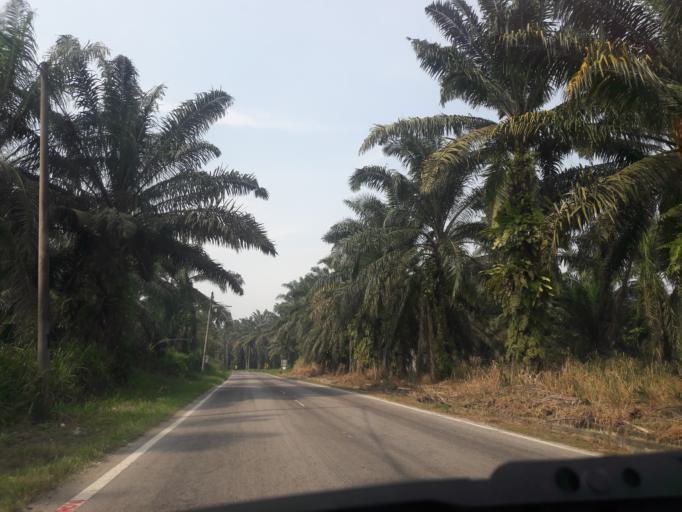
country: MY
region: Kedah
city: Kulim
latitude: 5.3490
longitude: 100.5196
